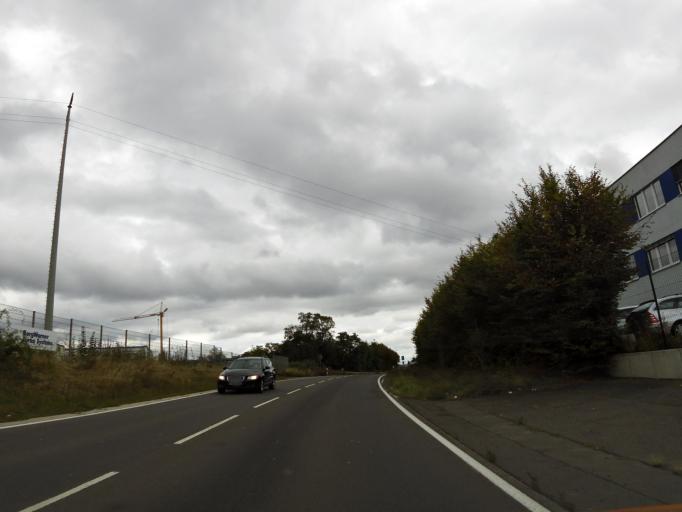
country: DE
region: Rheinland-Pfalz
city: Kirchheimbolanden
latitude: 49.6558
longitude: 8.0201
